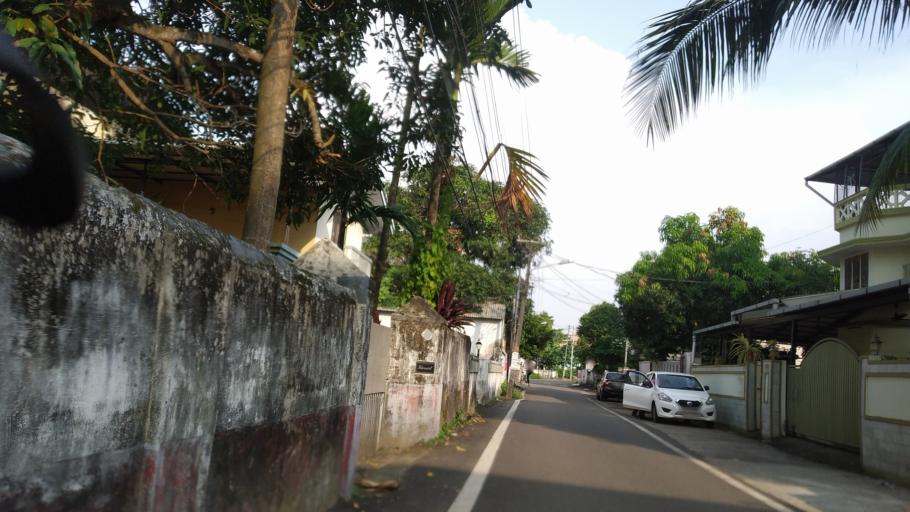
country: IN
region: Kerala
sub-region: Ernakulam
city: Cochin
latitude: 9.9861
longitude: 76.2900
